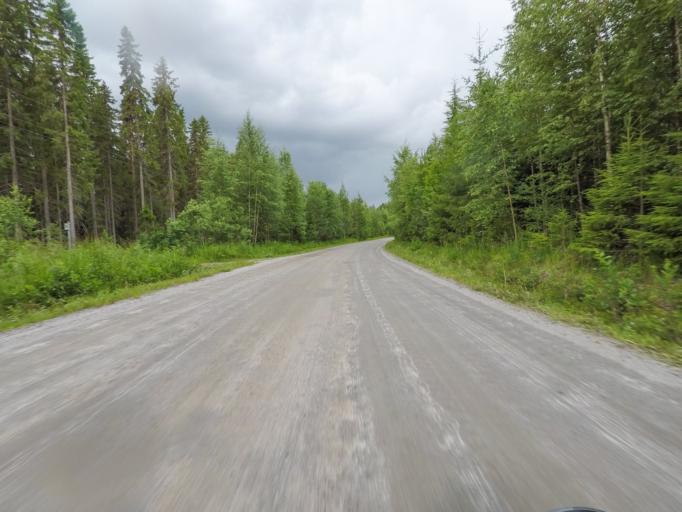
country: FI
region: Central Finland
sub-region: Jyvaeskylae
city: Hankasalmi
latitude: 62.4123
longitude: 26.6127
